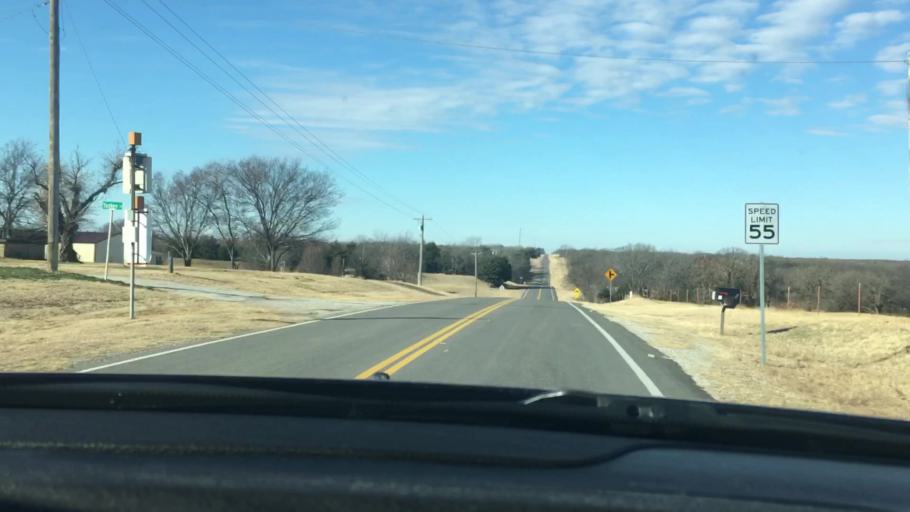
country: US
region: Oklahoma
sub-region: Love County
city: Marietta
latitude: 33.9405
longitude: -97.3214
